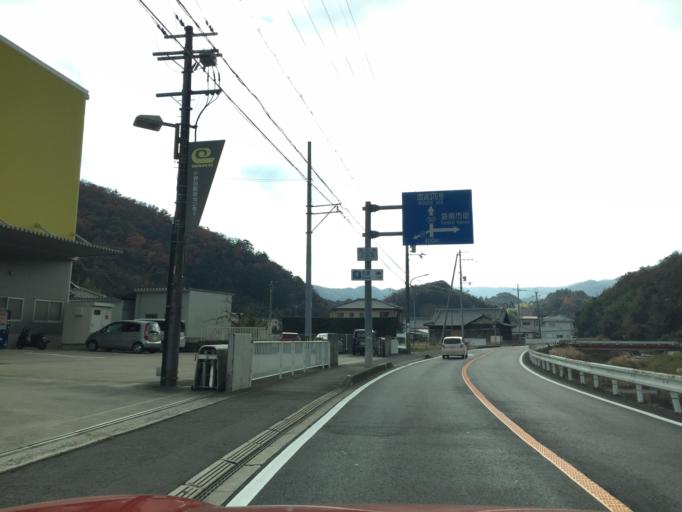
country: JP
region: Wakayama
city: Kainan
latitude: 34.1701
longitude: 135.2508
